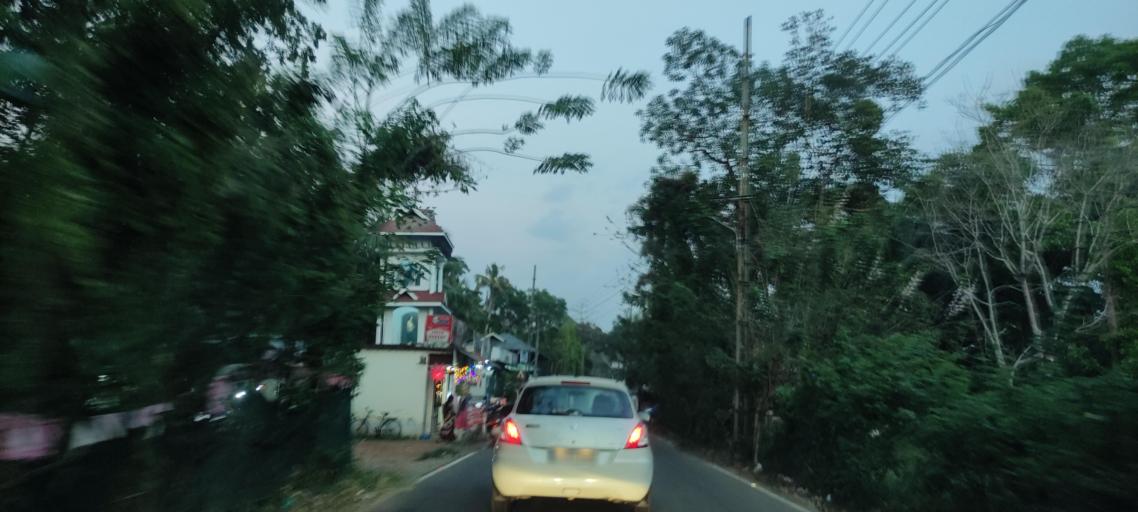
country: IN
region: Kerala
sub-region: Alappuzha
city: Kutiatodu
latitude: 9.7686
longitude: 76.3225
